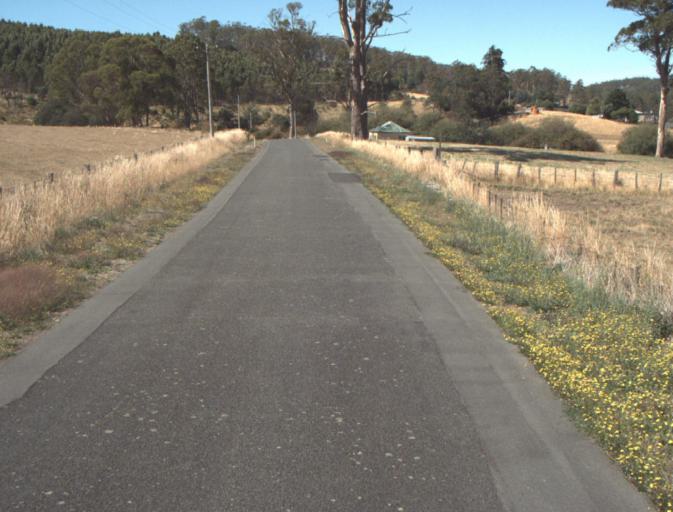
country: AU
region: Tasmania
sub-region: Launceston
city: Newstead
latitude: -41.3465
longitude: 147.3028
